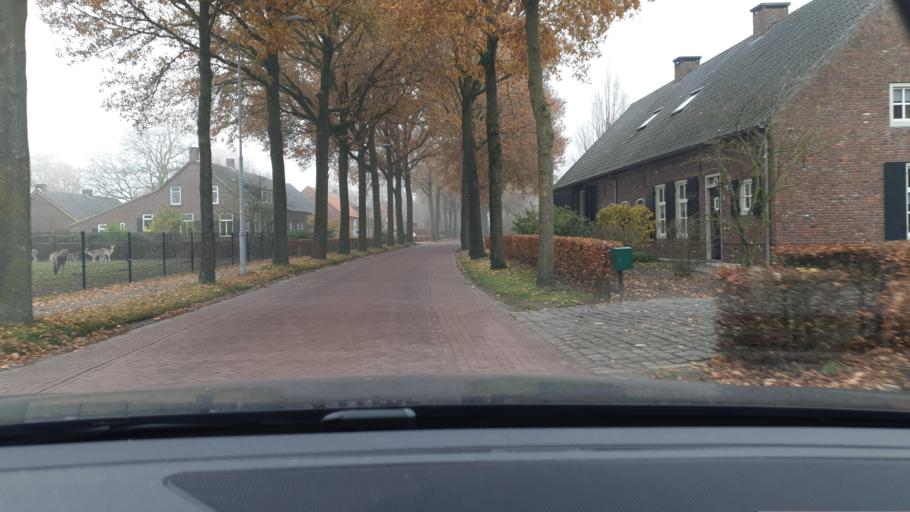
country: NL
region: North Brabant
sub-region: Gemeente Bladel en Netersel
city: Bladel
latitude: 51.3899
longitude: 5.1833
